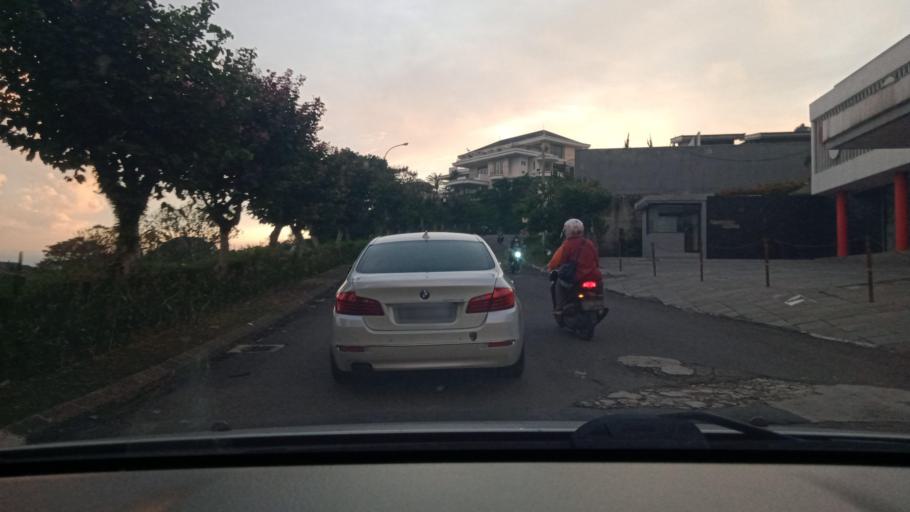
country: ID
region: West Java
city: Lembang
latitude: -6.8489
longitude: 107.5901
